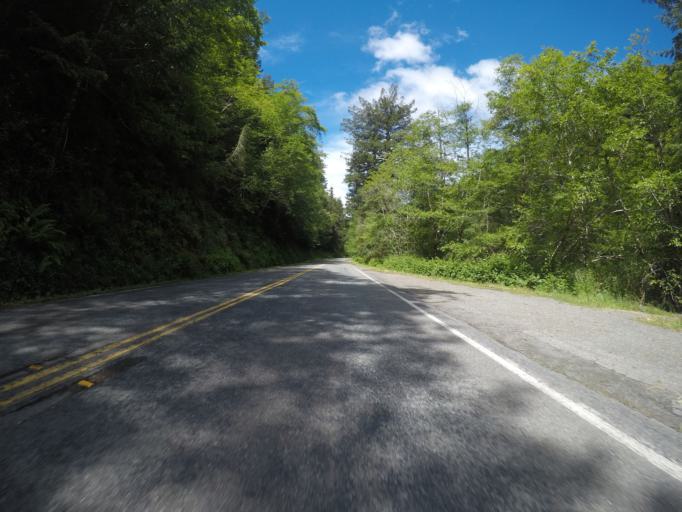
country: US
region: California
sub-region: Del Norte County
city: Bertsch-Oceanview
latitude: 41.7948
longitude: -124.0381
